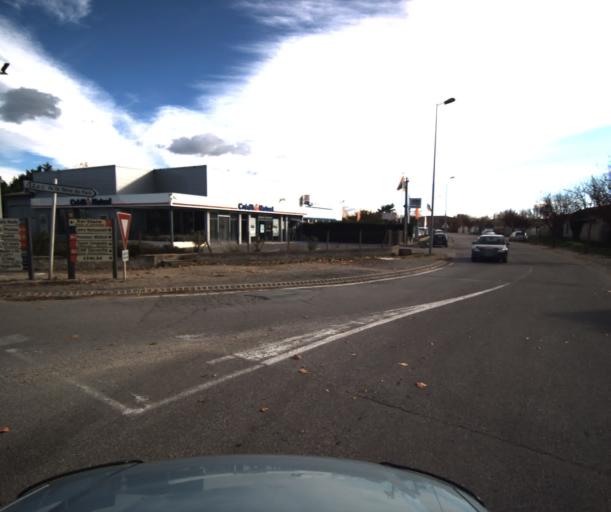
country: FR
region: Provence-Alpes-Cote d'Azur
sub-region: Departement du Vaucluse
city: Pertuis
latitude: 43.6781
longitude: 5.4989
